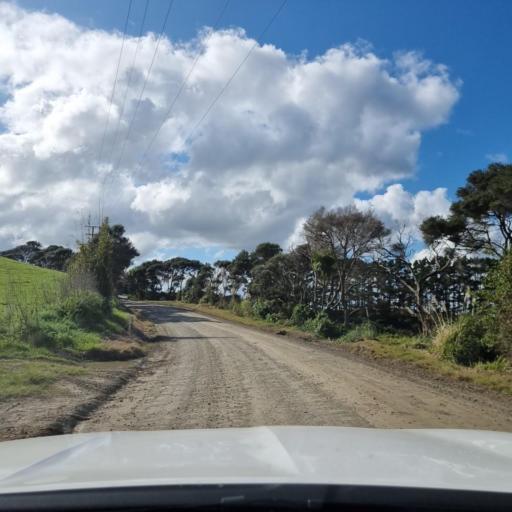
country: NZ
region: Auckland
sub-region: Auckland
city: Wellsford
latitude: -36.3181
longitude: 174.1348
